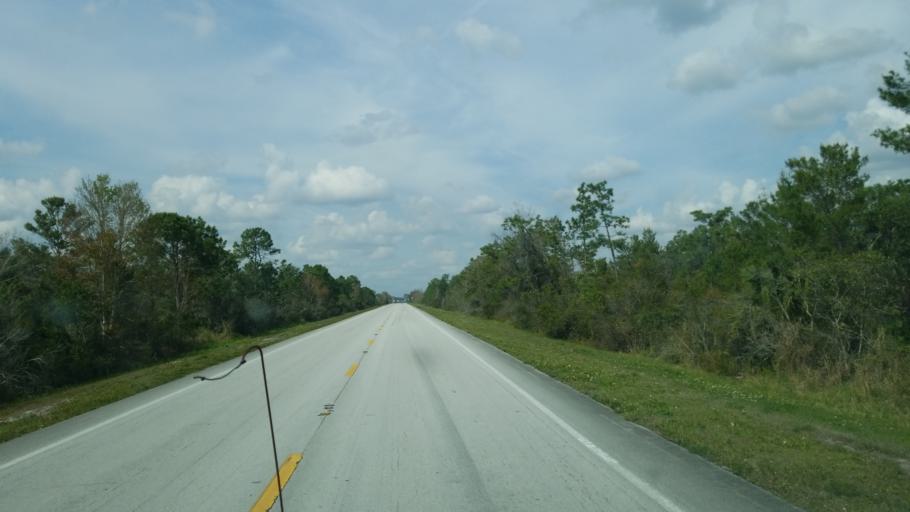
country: US
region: Florida
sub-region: Indian River County
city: Fellsmere
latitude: 27.6909
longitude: -80.8998
